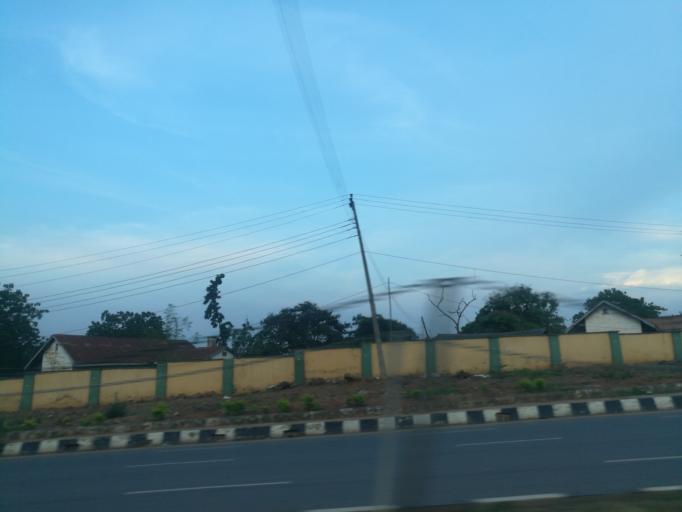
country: NG
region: Ogun
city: Abeokuta
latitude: 7.1708
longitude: 3.3710
